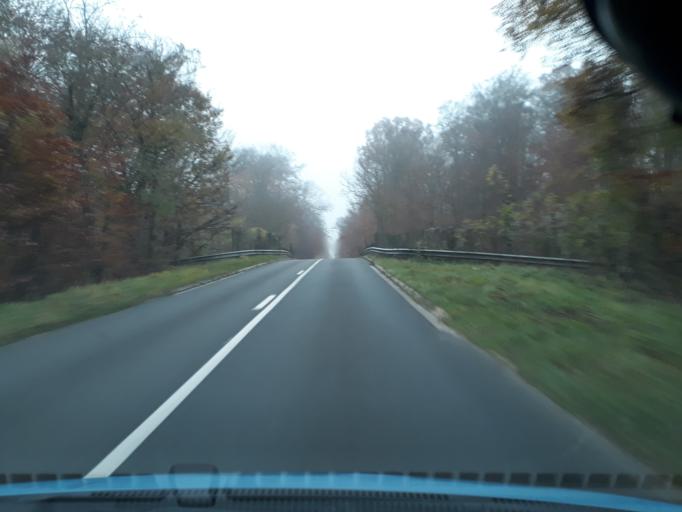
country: FR
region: Ile-de-France
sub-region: Departement de Seine-et-Marne
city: Thomery
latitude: 48.3944
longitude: 2.7682
